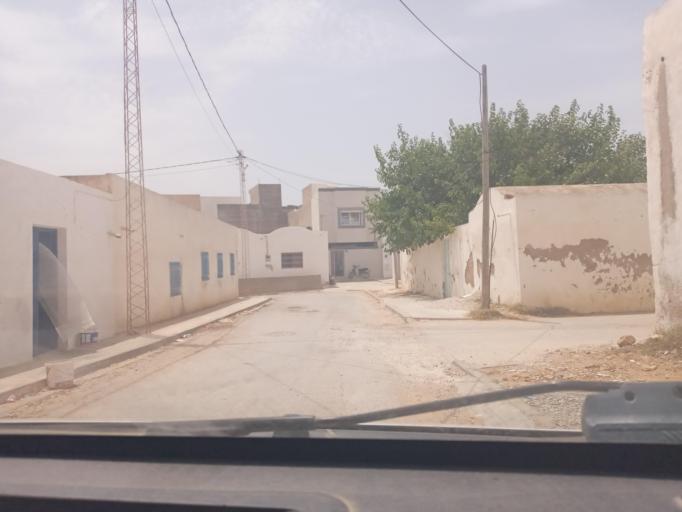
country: TN
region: Nabul
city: El Haouaria
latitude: 37.0517
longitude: 11.0142
